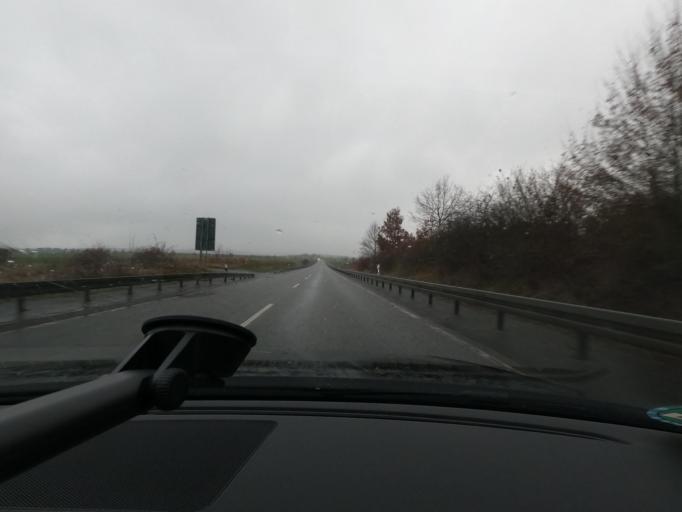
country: DE
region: Thuringia
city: Dingelstadt
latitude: 51.3119
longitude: 10.3281
